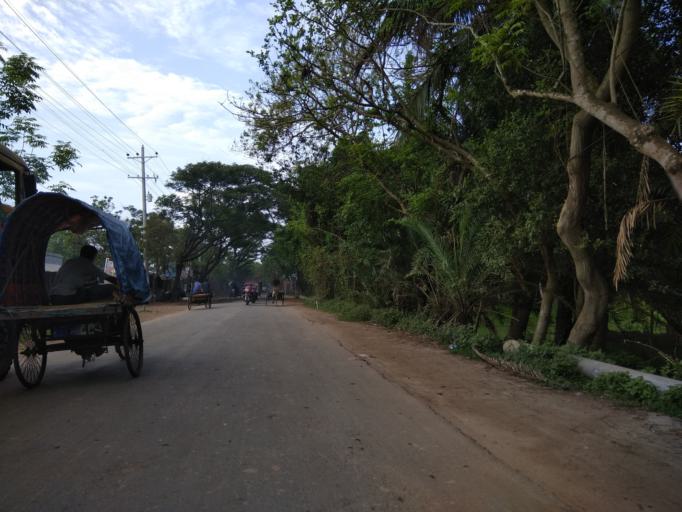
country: IN
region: West Bengal
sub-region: North 24 Parganas
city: Taki
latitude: 22.3413
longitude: 89.1054
